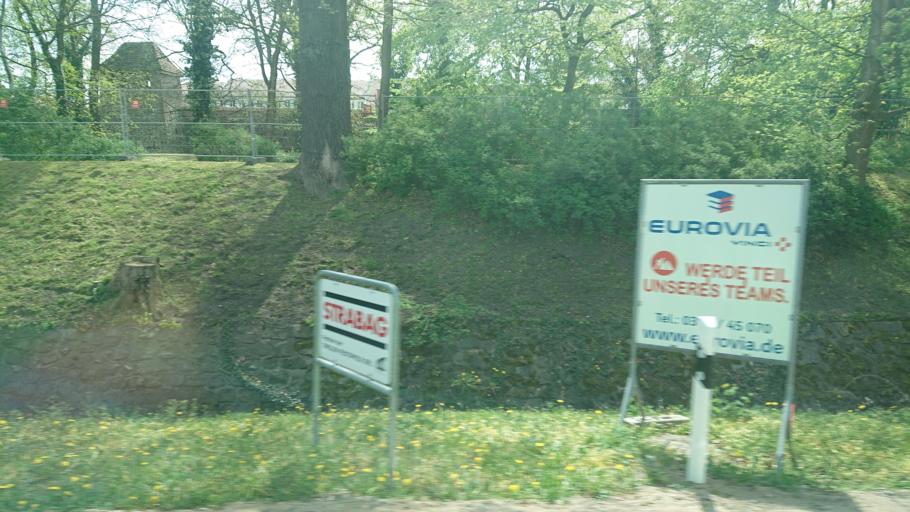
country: DE
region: Mecklenburg-Vorpommern
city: Neubrandenburg
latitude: 53.5608
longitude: 13.2625
